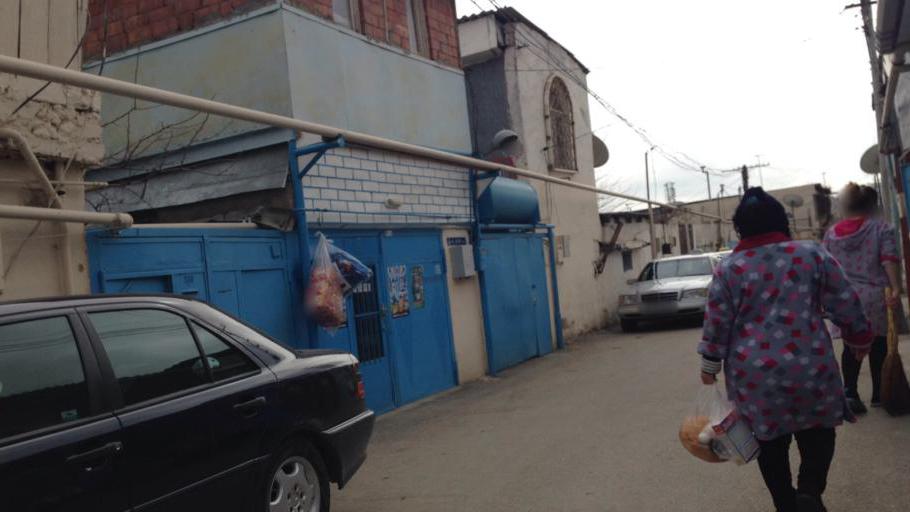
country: AZ
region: Baki
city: Bilajari
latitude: 40.4065
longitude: 49.8259
